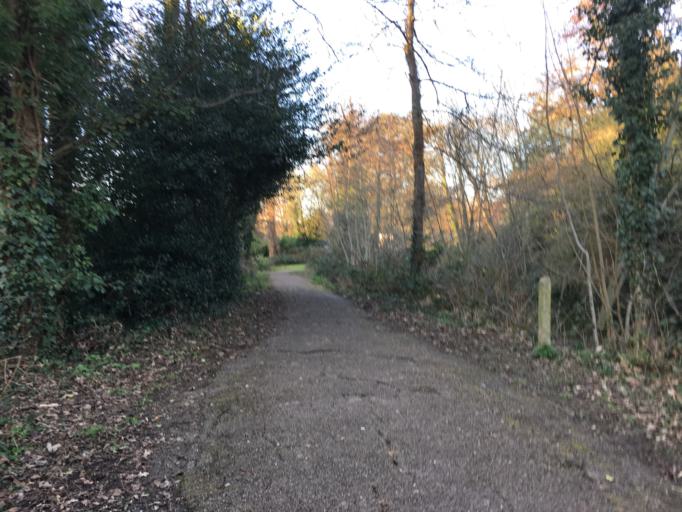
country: GB
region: England
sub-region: Greater London
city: Hendon
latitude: 51.5858
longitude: -0.2113
